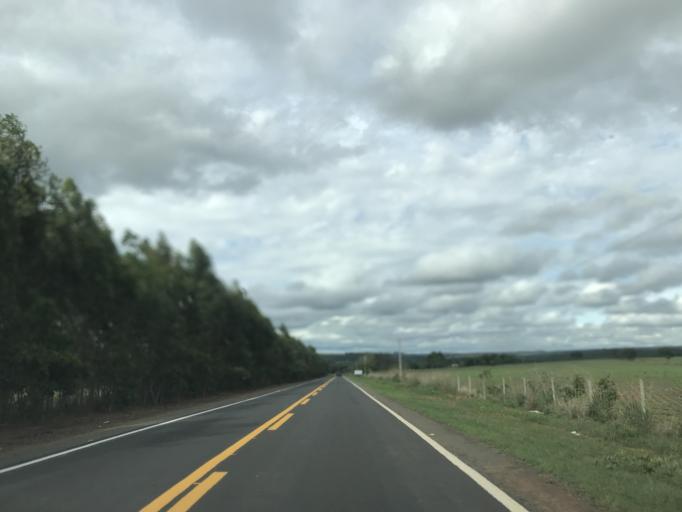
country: BR
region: Goias
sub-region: Bela Vista De Goias
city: Bela Vista de Goias
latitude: -17.1800
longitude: -48.6873
